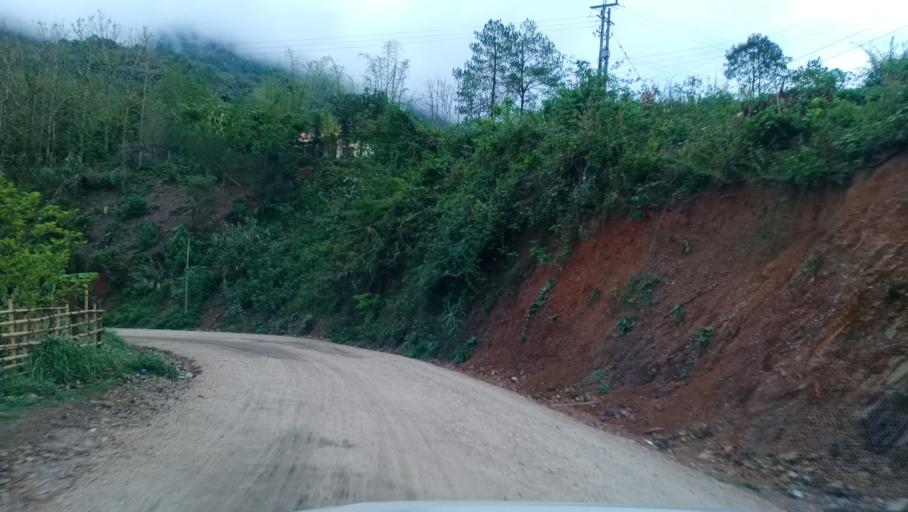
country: LA
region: Phongsali
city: Khoa
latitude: 21.1736
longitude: 102.7169
